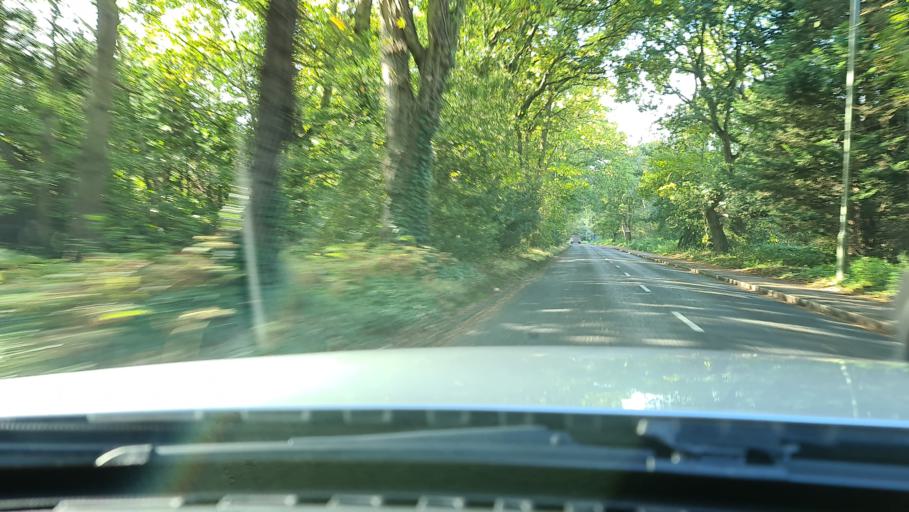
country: GB
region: England
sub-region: Surrey
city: Walton-on-Thames
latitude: 51.3699
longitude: -0.4155
